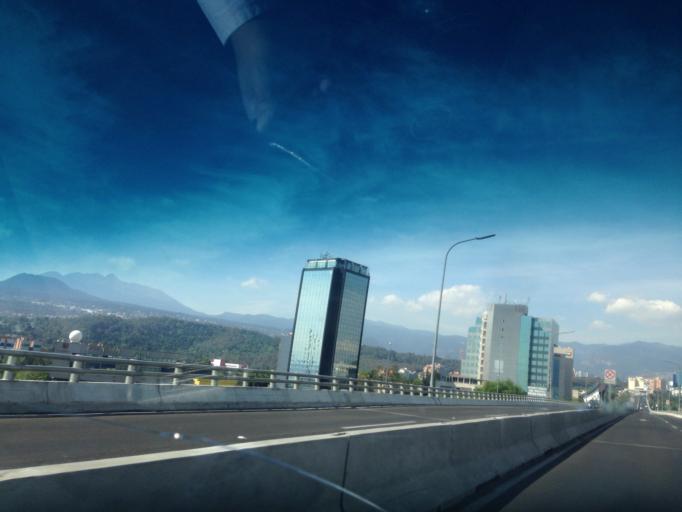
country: MX
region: Mexico City
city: Tlalpan
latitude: 19.3031
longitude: -99.1846
